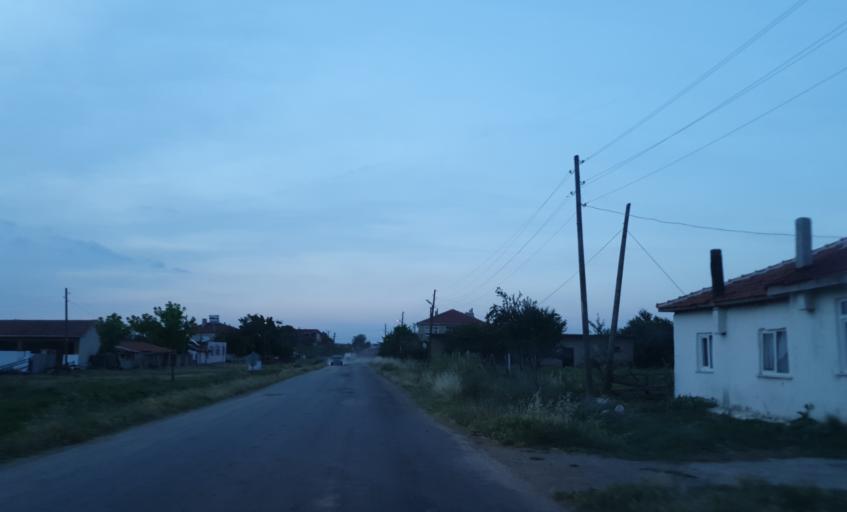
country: TR
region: Kirklareli
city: Vize
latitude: 41.4832
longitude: 27.7524
